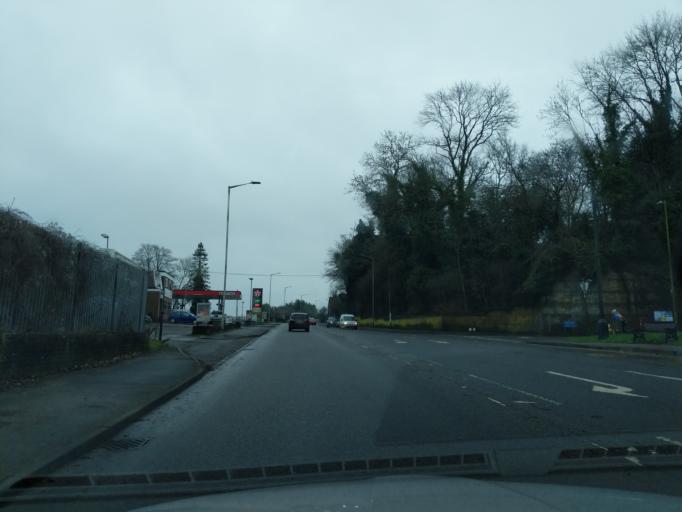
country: GB
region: England
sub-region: Hertfordshire
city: Kings Langley
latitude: 51.7266
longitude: -0.4540
